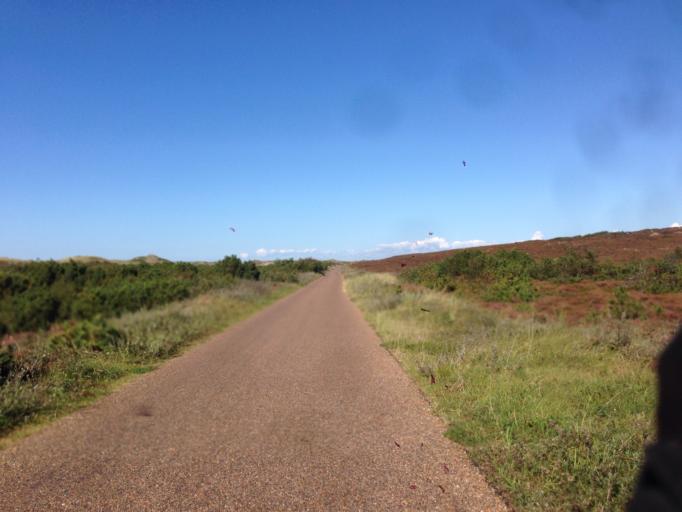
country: DE
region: Schleswig-Holstein
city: Tinnum
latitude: 54.9792
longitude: 8.3573
